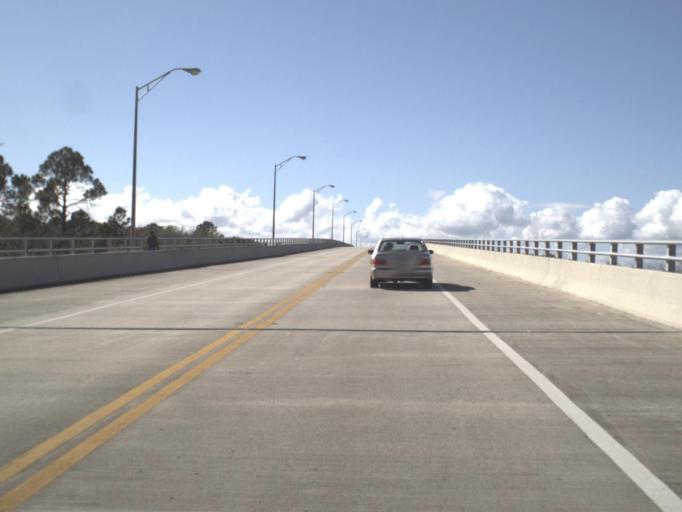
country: US
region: Florida
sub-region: Flagler County
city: Palm Coast
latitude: 29.5752
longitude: -81.1862
